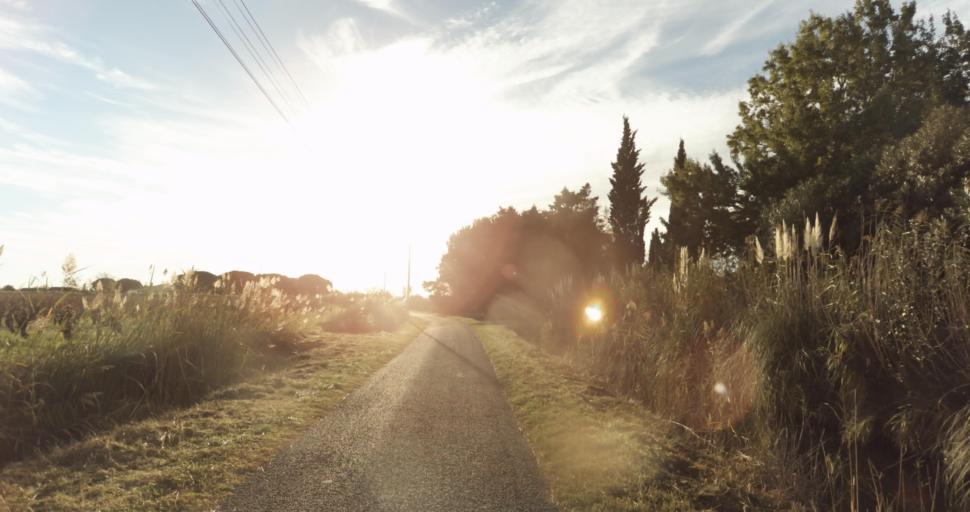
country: FR
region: Languedoc-Roussillon
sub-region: Departement du Gard
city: Aigues-Mortes
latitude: 43.5555
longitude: 4.2082
